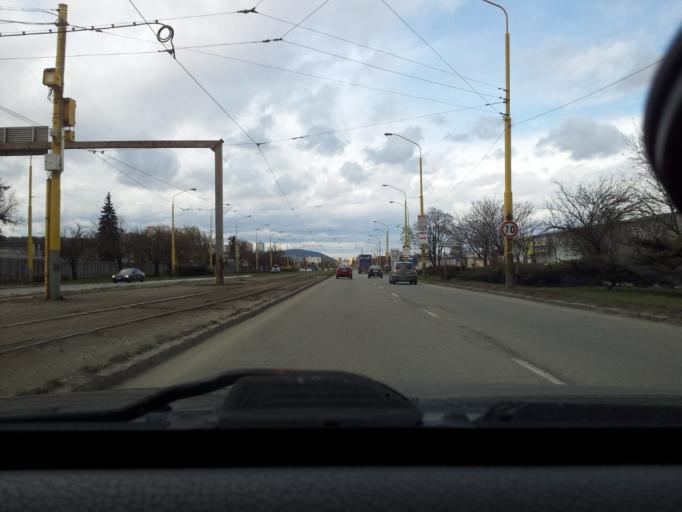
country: SK
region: Kosicky
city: Kosice
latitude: 48.6896
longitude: 21.2660
